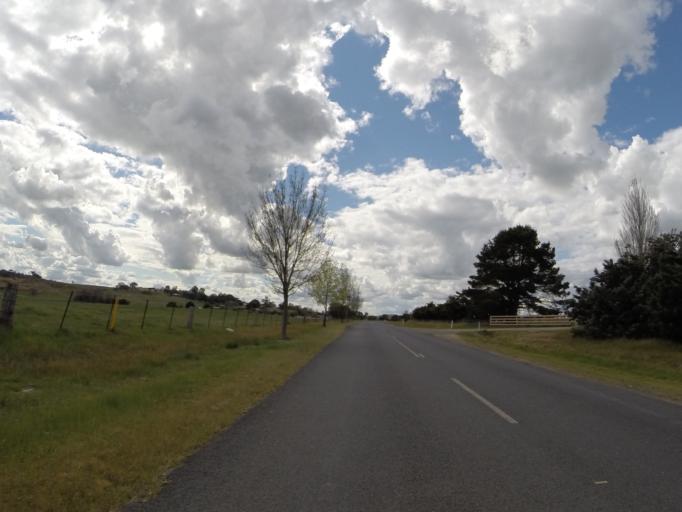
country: AU
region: New South Wales
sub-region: Yass Valley
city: Yass
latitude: -34.8624
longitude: 148.9164
